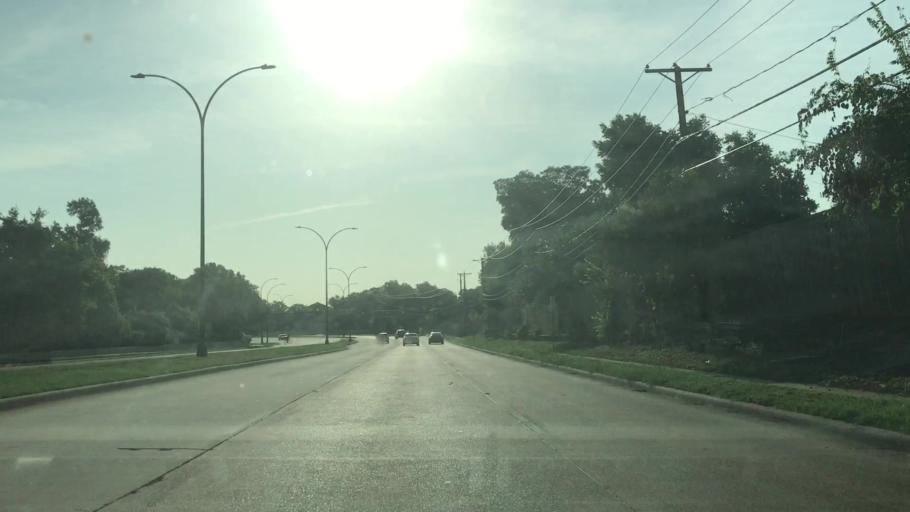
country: US
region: Texas
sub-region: Tarrant County
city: Arlington
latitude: 32.7822
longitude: -97.1184
